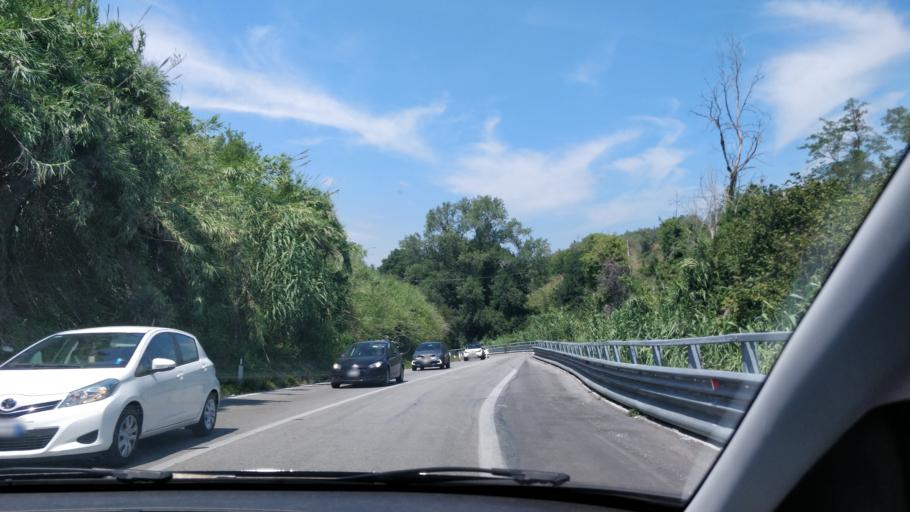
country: IT
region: Abruzzo
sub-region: Provincia di Chieti
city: Ortona
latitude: 42.3368
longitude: 14.4138
